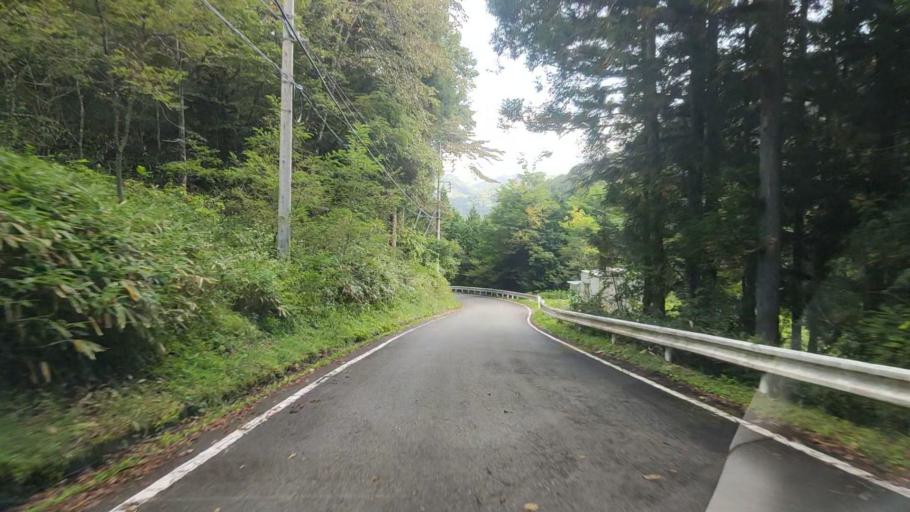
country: JP
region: Gunma
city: Nakanojomachi
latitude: 36.6524
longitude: 138.6362
